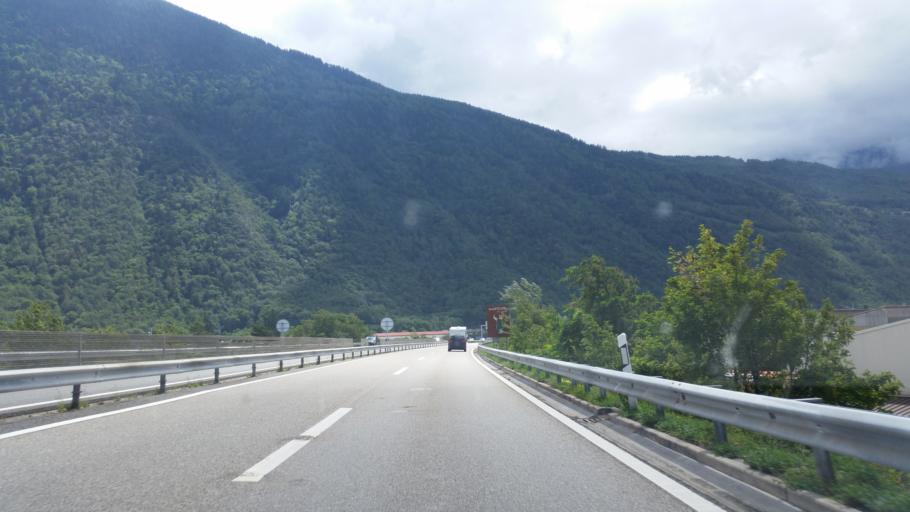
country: CH
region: Valais
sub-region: Martigny District
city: Martigny-Ville
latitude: 46.1101
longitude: 7.0973
